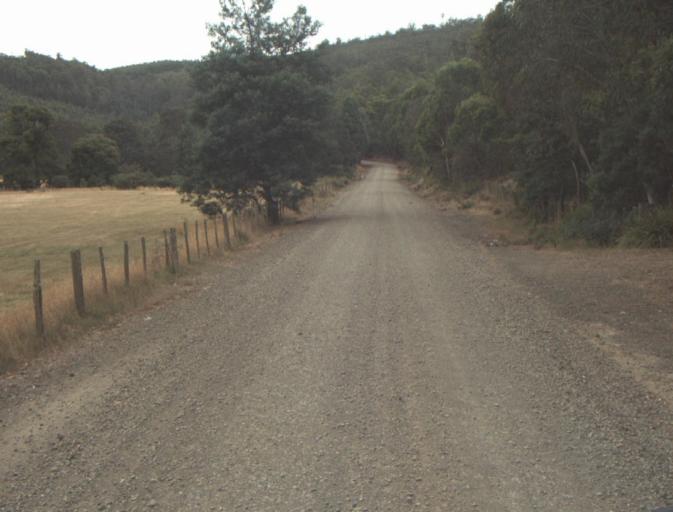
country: AU
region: Tasmania
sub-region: Northern Midlands
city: Evandale
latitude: -41.4636
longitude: 147.4956
